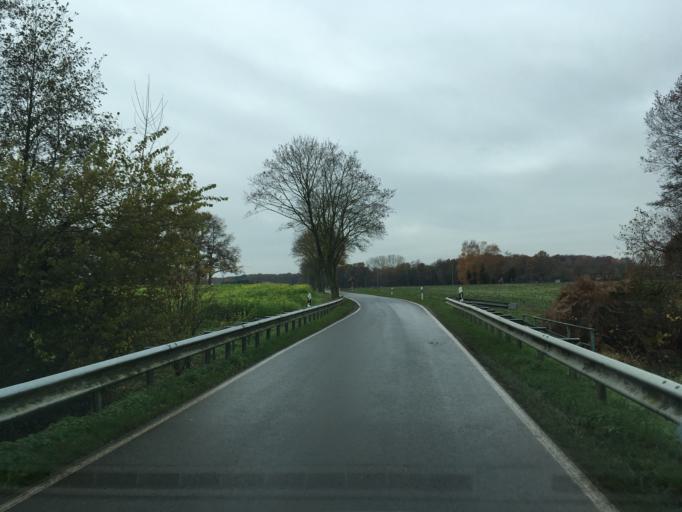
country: DE
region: North Rhine-Westphalia
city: Stadtlohn
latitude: 52.0100
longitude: 6.9495
